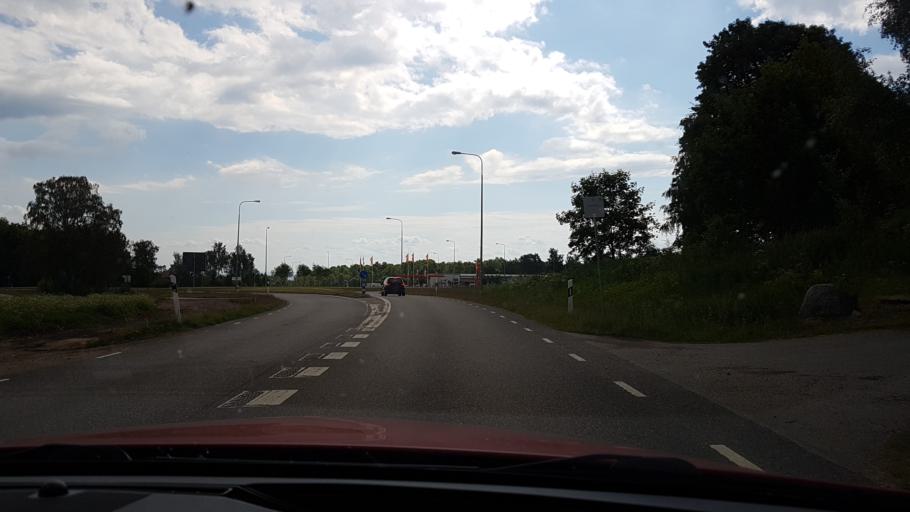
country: SE
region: Vaestra Goetaland
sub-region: Hjo Kommun
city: Hjo
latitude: 58.3040
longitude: 14.2522
